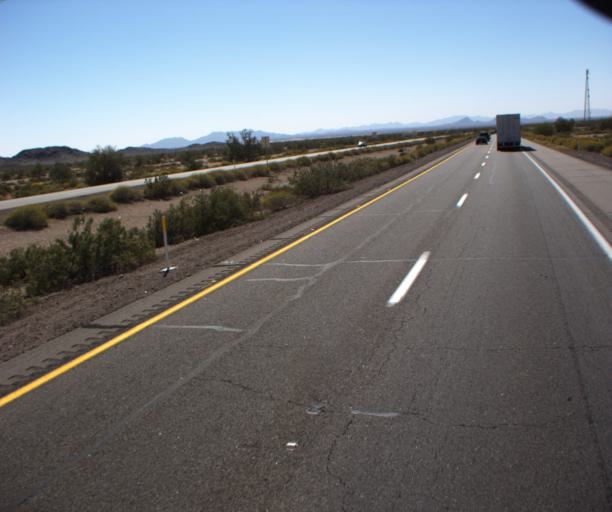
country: US
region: Arizona
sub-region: Yuma County
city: Wellton
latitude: 32.7250
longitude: -113.7549
